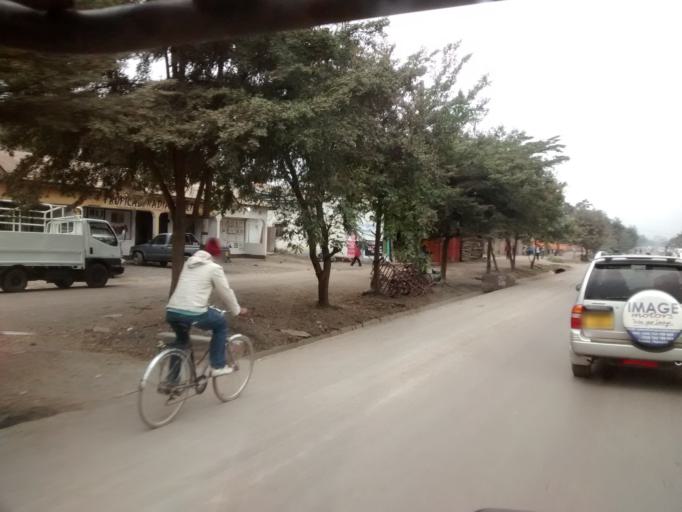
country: TZ
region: Arusha
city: Arusha
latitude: -3.3758
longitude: 36.6679
